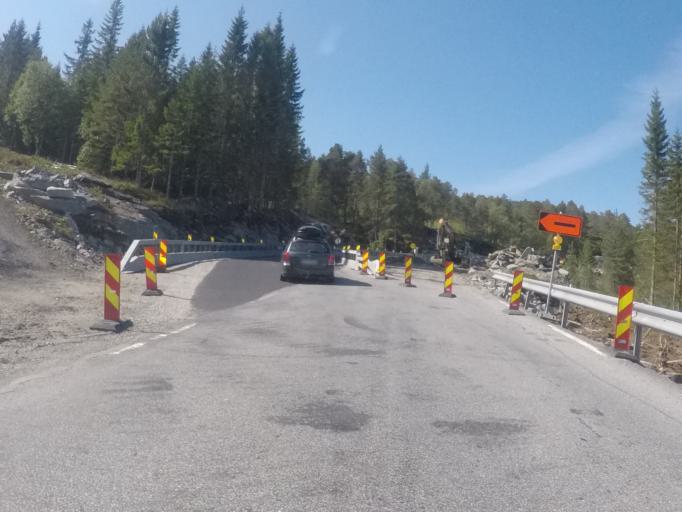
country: NO
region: Sogn og Fjordane
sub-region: Hornindal
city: Hornindal
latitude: 61.7926
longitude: 6.5101
